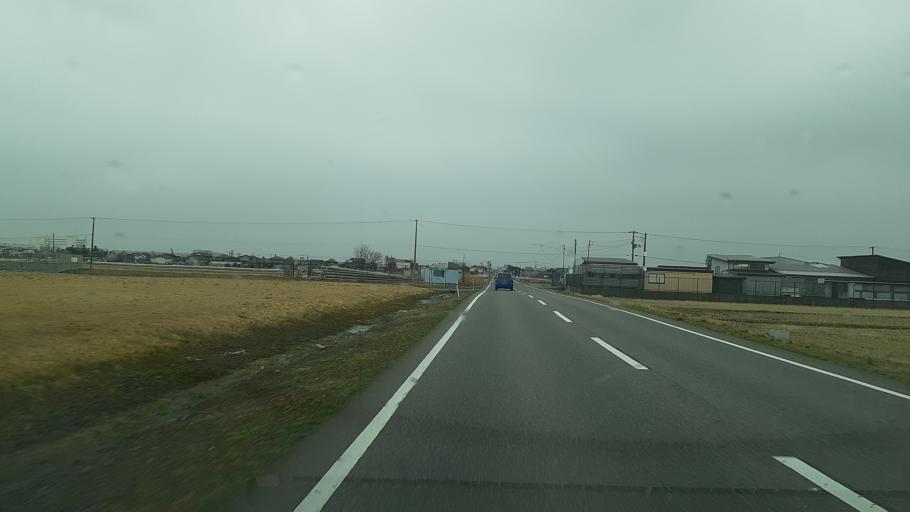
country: JP
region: Niigata
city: Kameda-honcho
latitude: 37.8640
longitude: 139.0722
